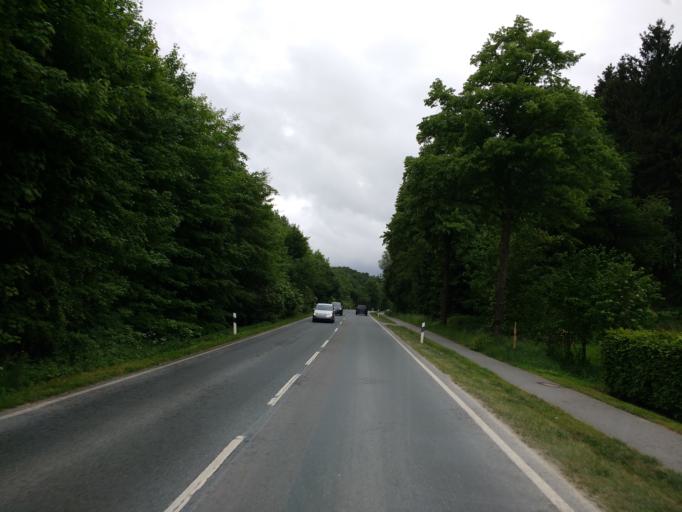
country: DE
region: Lower Saxony
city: Hilter
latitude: 52.1530
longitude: 8.1536
